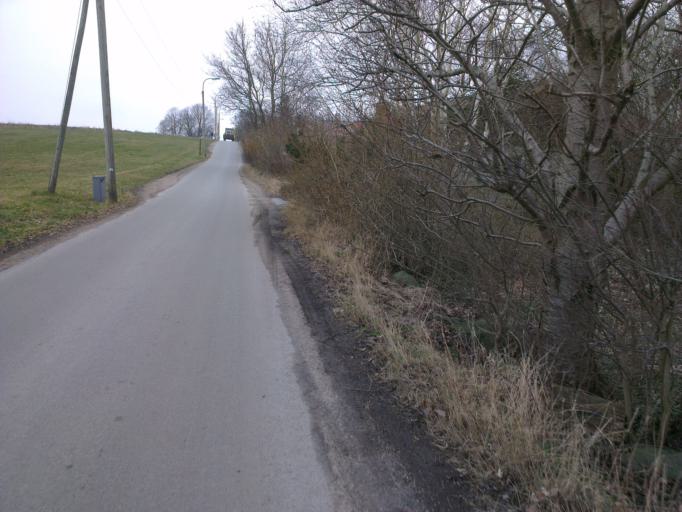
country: DK
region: Capital Region
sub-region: Egedal Kommune
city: Olstykke
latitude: 55.8116
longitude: 12.1130
